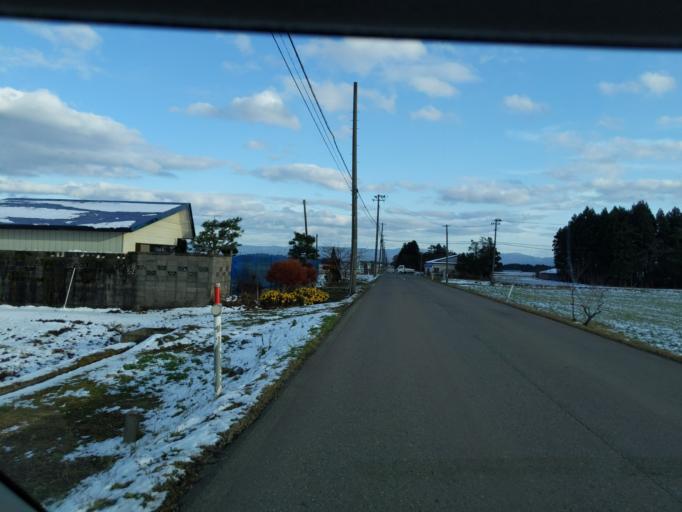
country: JP
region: Iwate
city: Kitakami
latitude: 39.2129
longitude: 141.0283
